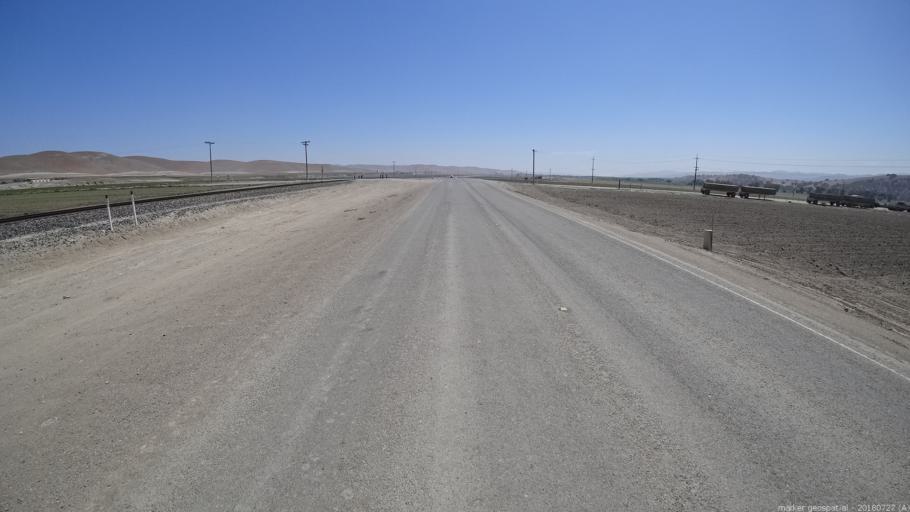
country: US
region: California
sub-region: Monterey County
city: King City
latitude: 36.0946
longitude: -120.9630
